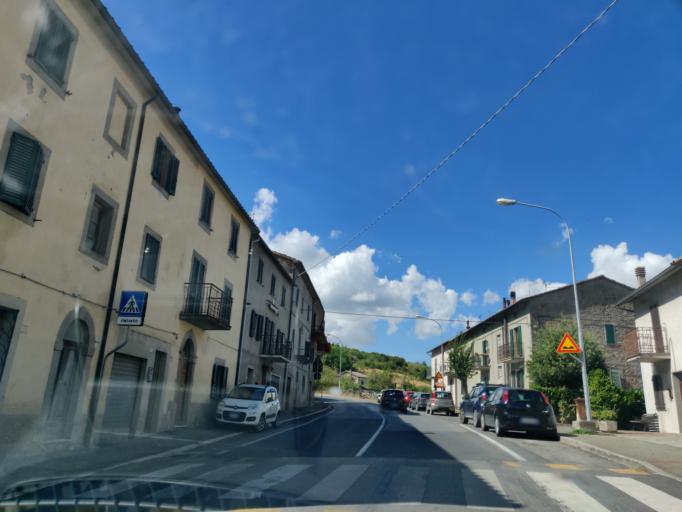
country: IT
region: Tuscany
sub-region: Provincia di Siena
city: Abbadia San Salvatore
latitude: 42.8885
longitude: 11.6669
